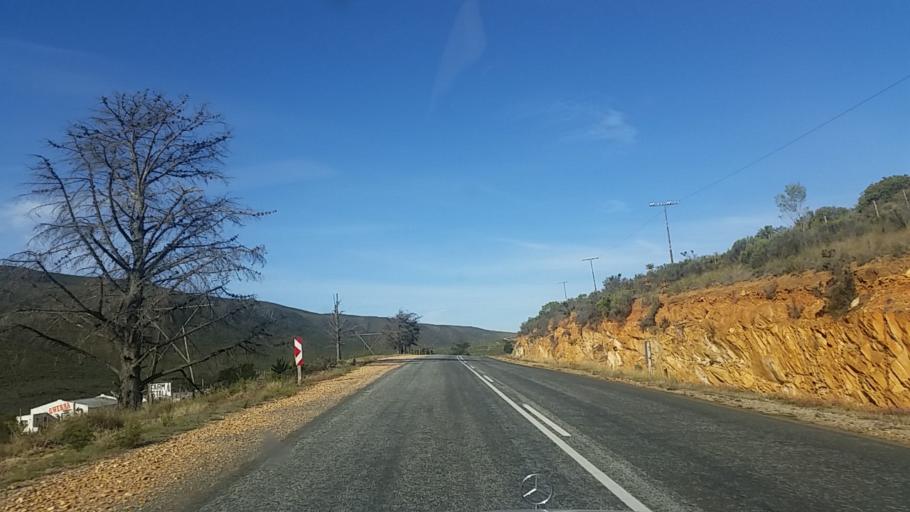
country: ZA
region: Western Cape
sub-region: Eden District Municipality
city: Knysna
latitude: -33.7449
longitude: 22.9903
